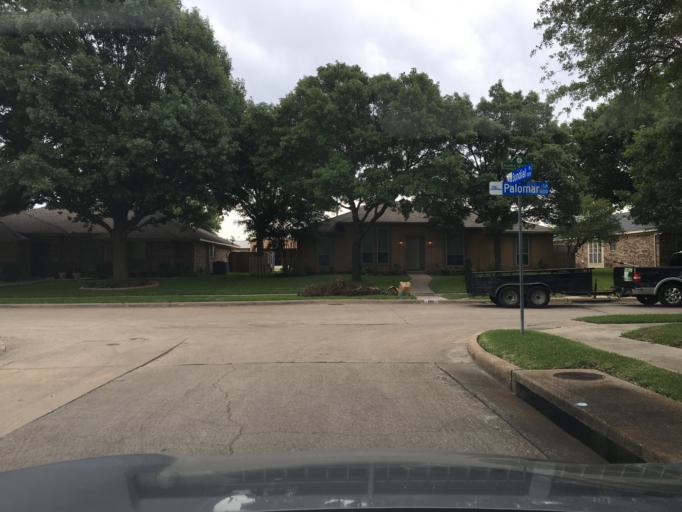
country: US
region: Texas
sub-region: Dallas County
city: Richardson
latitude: 32.9396
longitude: -96.7073
